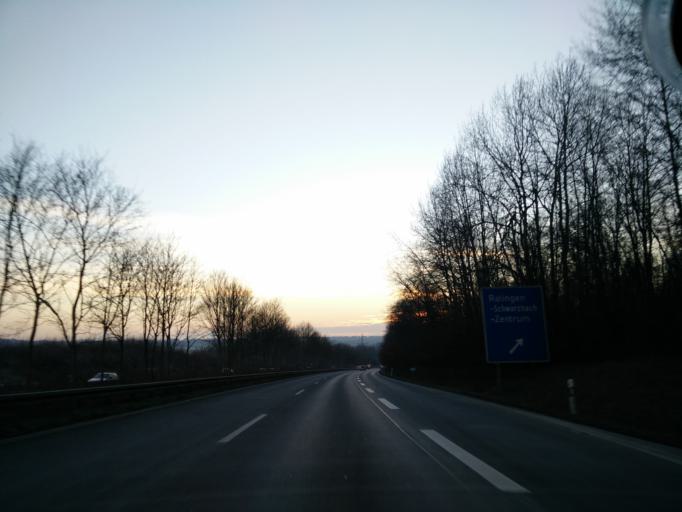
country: DE
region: North Rhine-Westphalia
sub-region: Regierungsbezirk Dusseldorf
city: Ratingen
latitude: 51.2891
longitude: 6.8770
